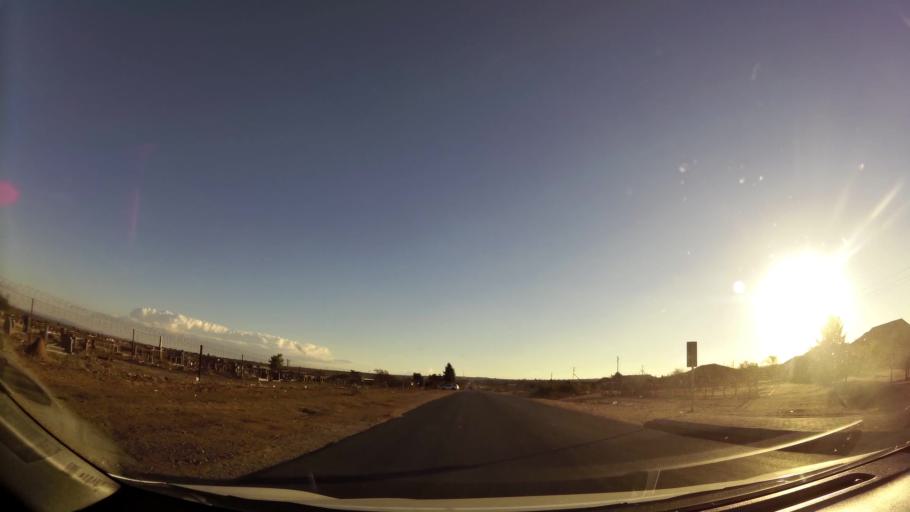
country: ZA
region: Limpopo
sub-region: Capricorn District Municipality
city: Polokwane
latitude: -23.8366
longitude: 29.3595
